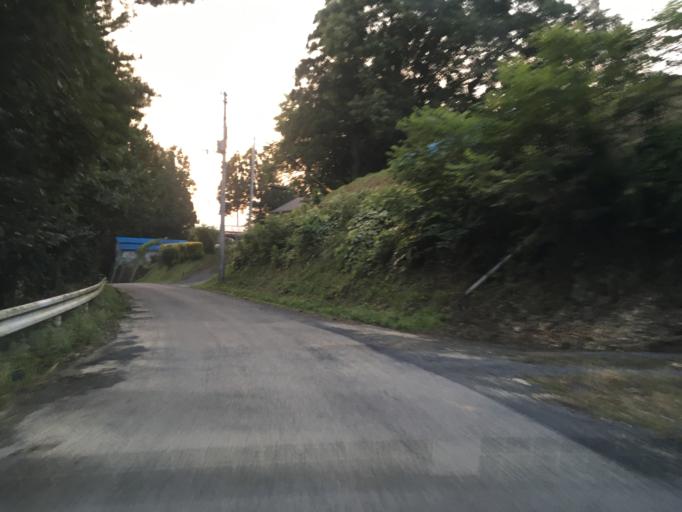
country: JP
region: Iwate
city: Ichinoseki
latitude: 38.8431
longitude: 141.2862
